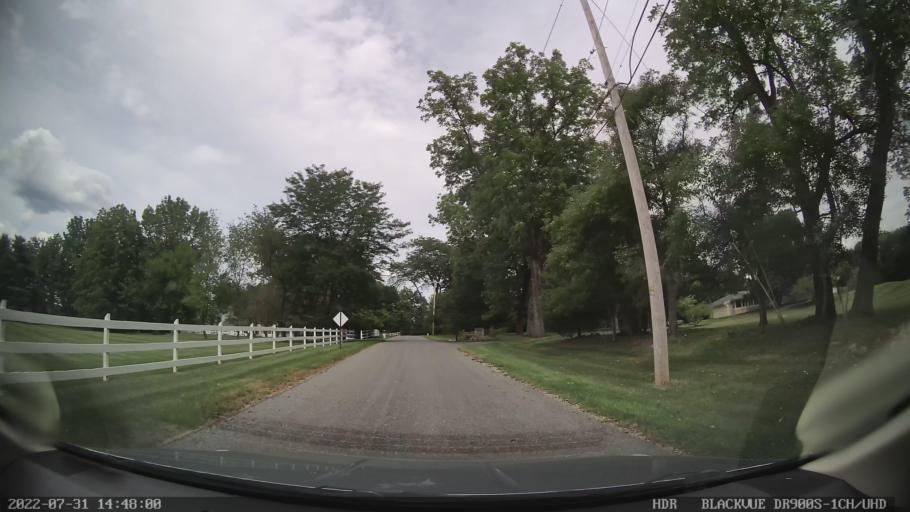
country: US
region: Pennsylvania
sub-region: Northampton County
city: Hellertown
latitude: 40.5716
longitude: -75.3664
